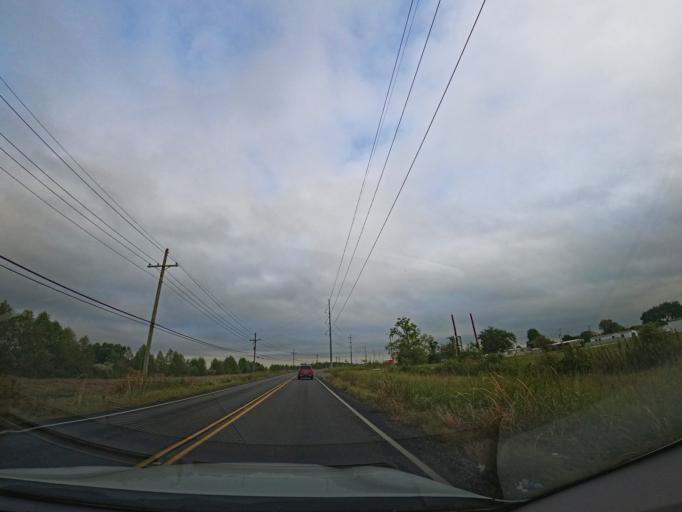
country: US
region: Louisiana
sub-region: Terrebonne Parish
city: Presquille
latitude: 29.5334
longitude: -90.6755
